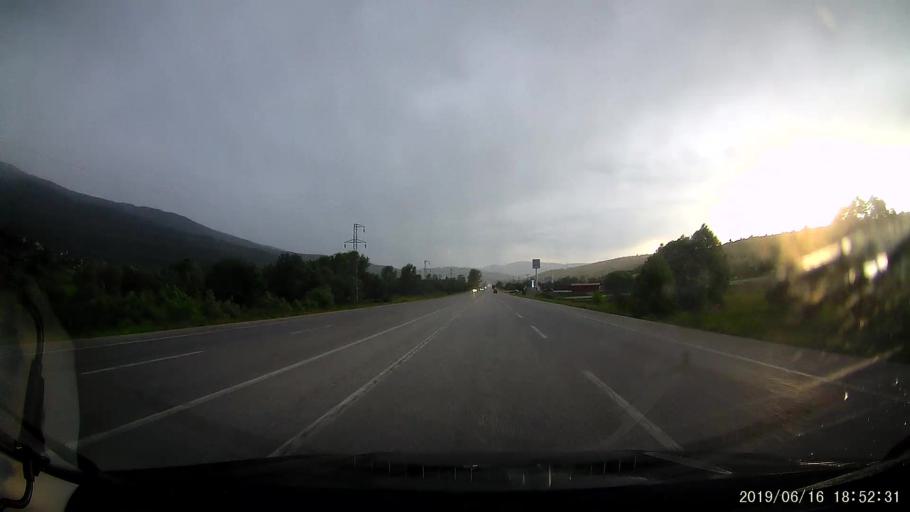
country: TR
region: Erzincan
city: Catalcam
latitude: 39.9023
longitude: 38.8995
